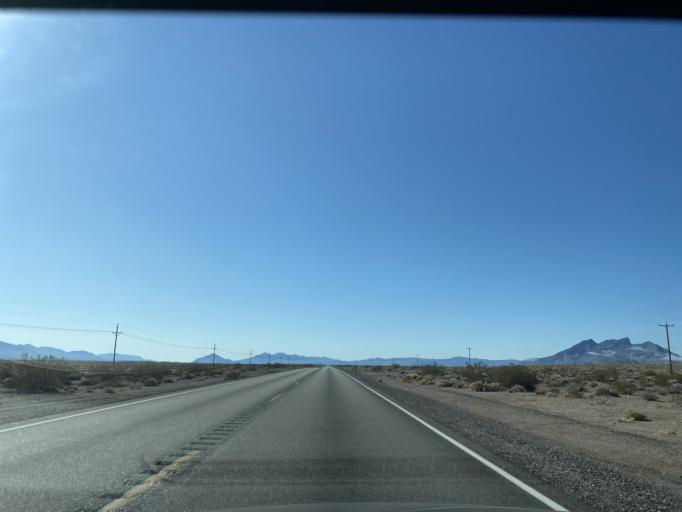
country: US
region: Nevada
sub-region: Nye County
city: Pahrump
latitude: 36.4664
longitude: -116.4217
